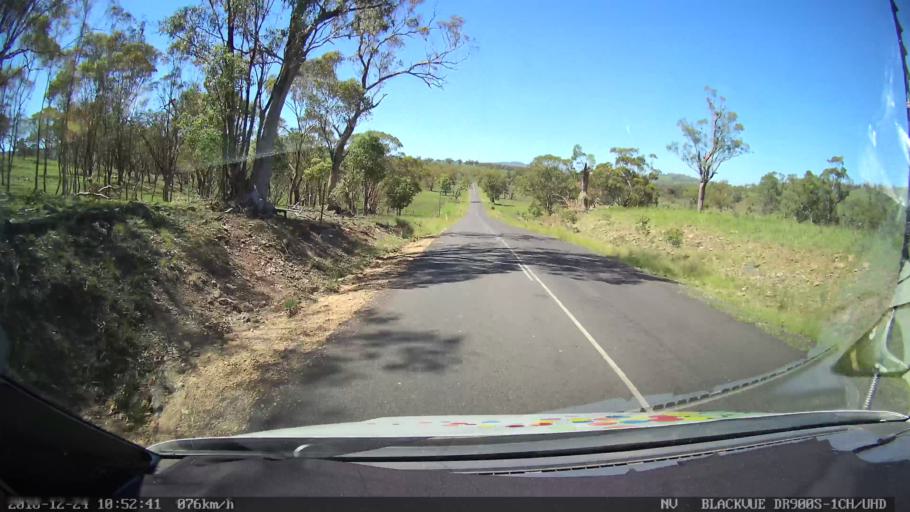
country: AU
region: New South Wales
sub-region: Upper Hunter Shire
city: Merriwa
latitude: -31.9832
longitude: 150.4224
